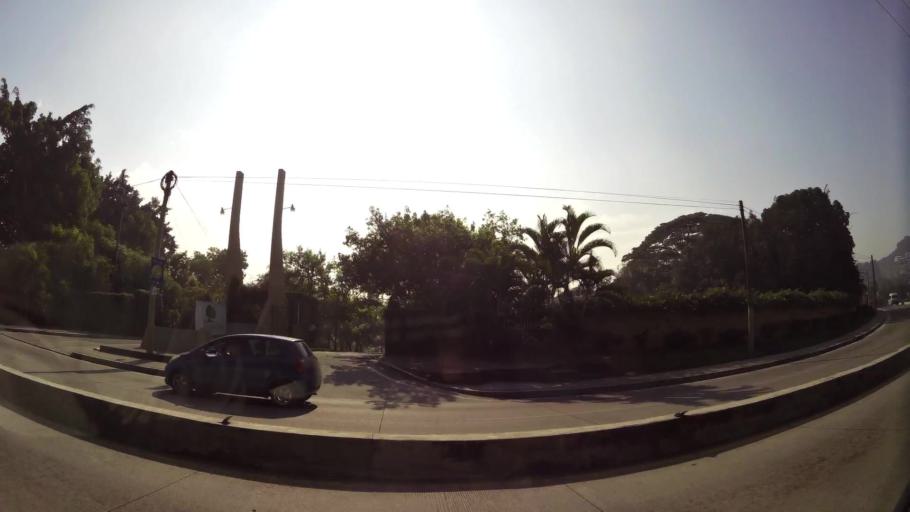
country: SV
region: La Libertad
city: Antiguo Cuscatlan
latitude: 13.6718
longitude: -89.2225
